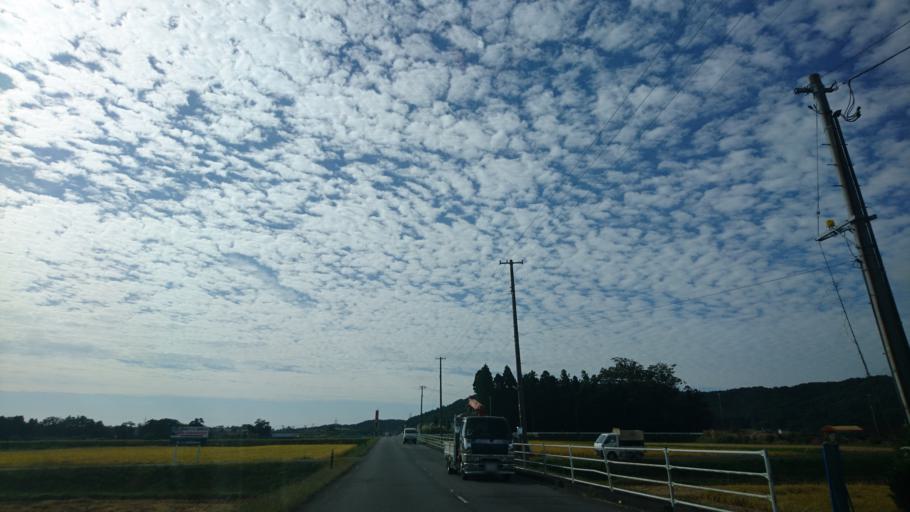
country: JP
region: Fukushima
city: Sukagawa
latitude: 37.3247
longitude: 140.2669
